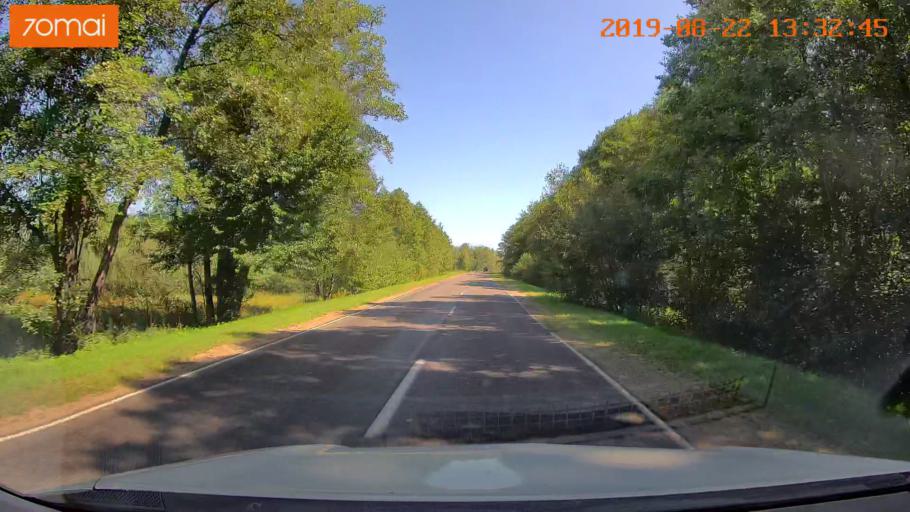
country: BY
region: Minsk
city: Staryya Darohi
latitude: 53.2170
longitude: 28.2117
